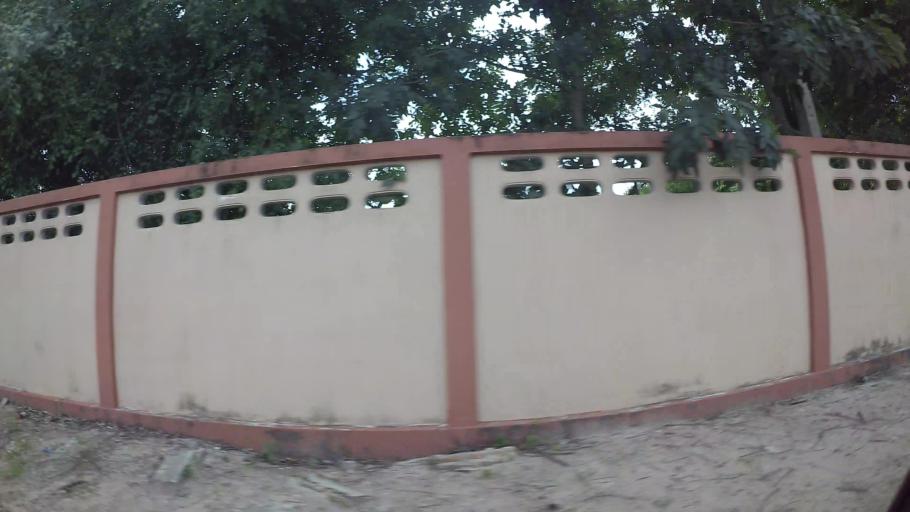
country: TH
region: Chon Buri
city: Si Racha
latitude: 13.1619
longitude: 100.9827
